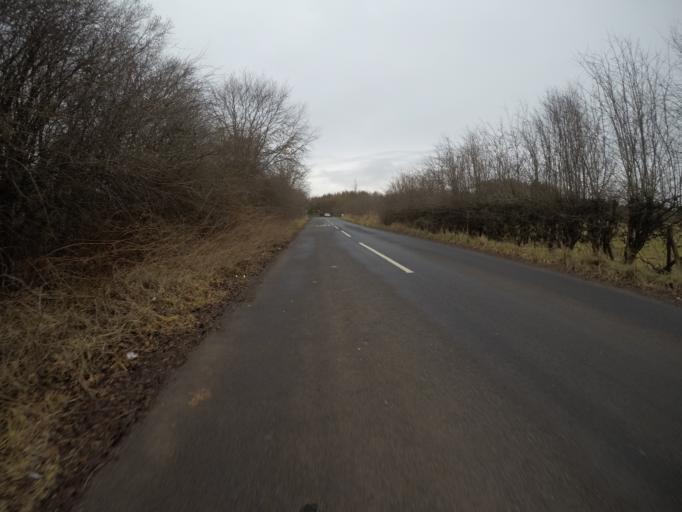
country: GB
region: Scotland
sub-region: North Ayrshire
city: Kilwinning
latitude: 55.6389
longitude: -4.6908
